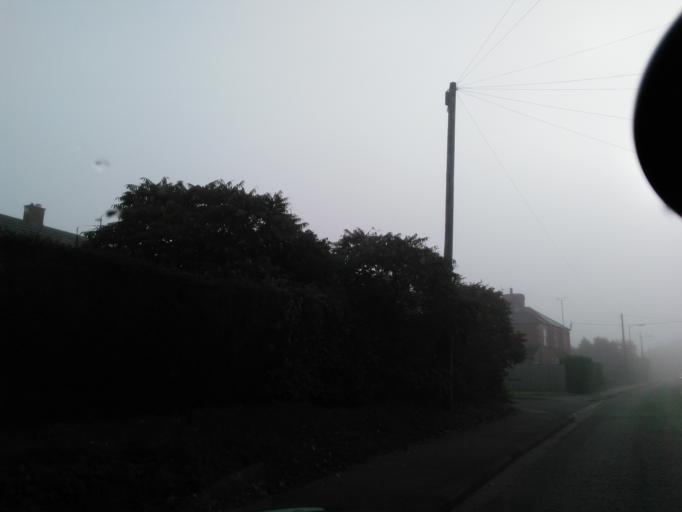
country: GB
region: England
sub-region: Wiltshire
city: Devizes
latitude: 51.3468
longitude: -1.9821
